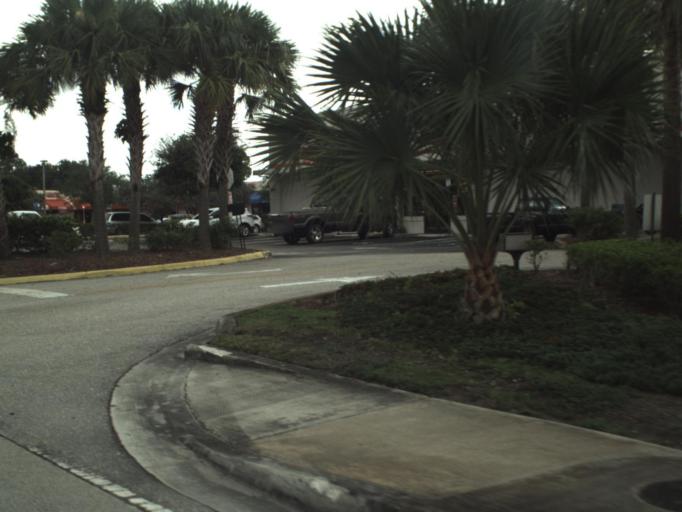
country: US
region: Florida
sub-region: Palm Beach County
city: Greenacres City
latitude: 26.6086
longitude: -80.1468
